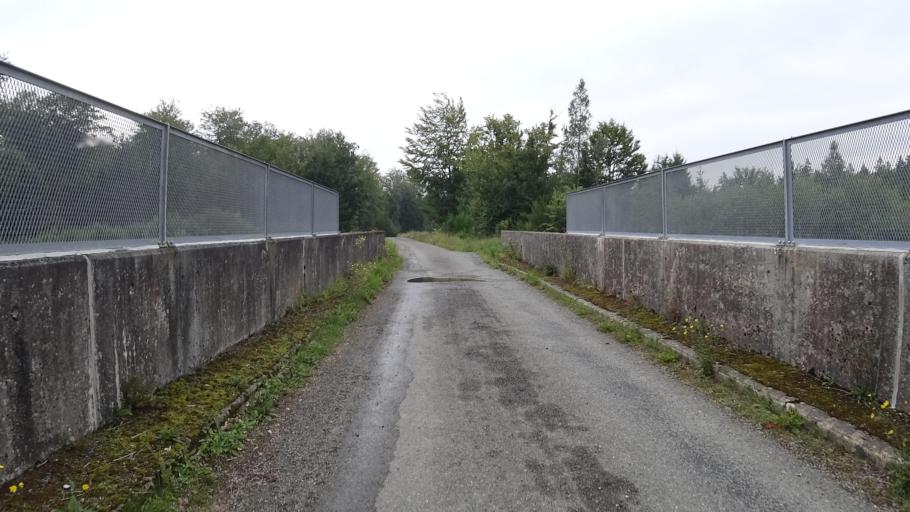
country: BE
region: Wallonia
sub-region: Province du Luxembourg
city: Chiny
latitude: 49.7873
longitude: 5.3255
